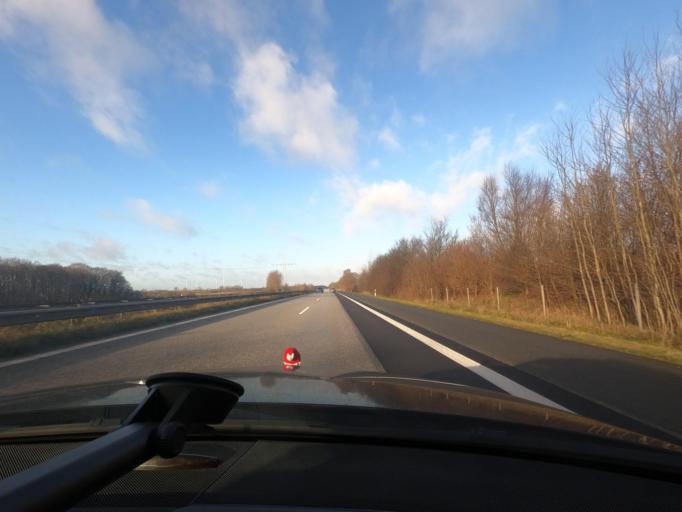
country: DE
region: Schleswig-Holstein
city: Bollingstedt
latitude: 54.5914
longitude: 9.4608
